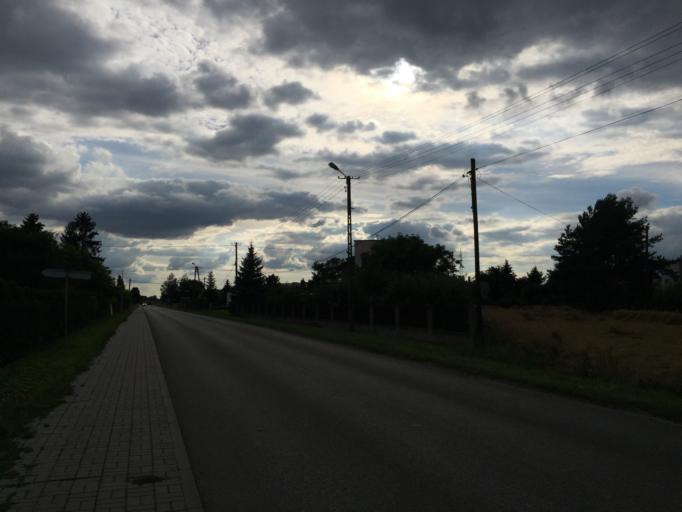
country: PL
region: Lesser Poland Voivodeship
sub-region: Powiat oswiecimski
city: Brzezinka
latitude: 50.0357
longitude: 19.1878
